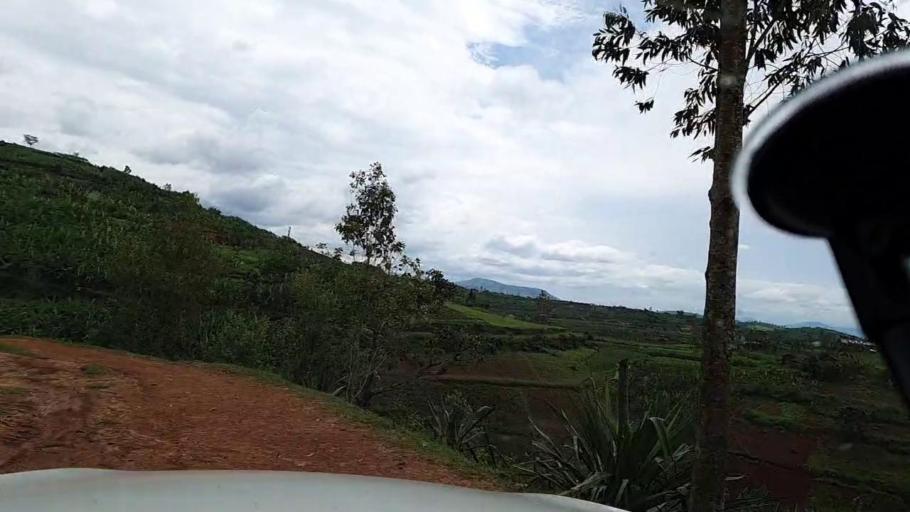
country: RW
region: Southern Province
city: Gitarama
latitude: -2.0723
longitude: 29.6431
